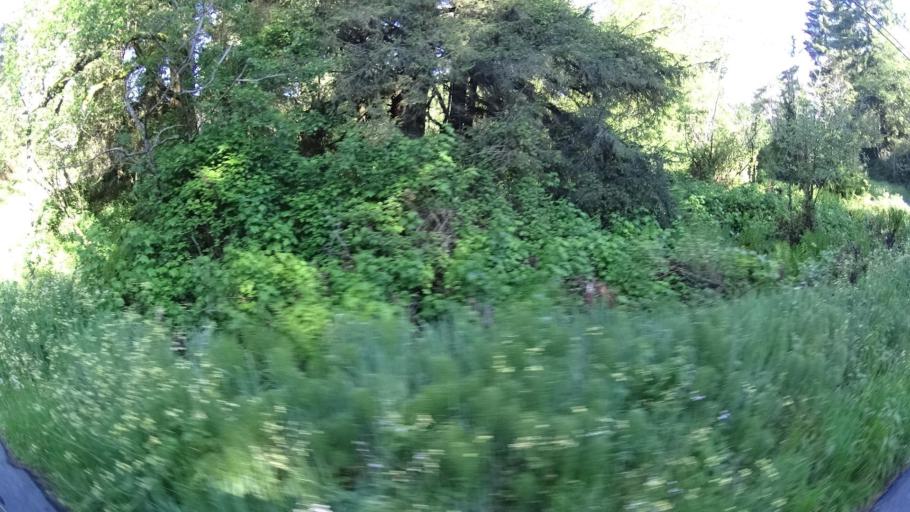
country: US
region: California
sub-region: Humboldt County
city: McKinleyville
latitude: 40.9948
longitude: -124.0992
